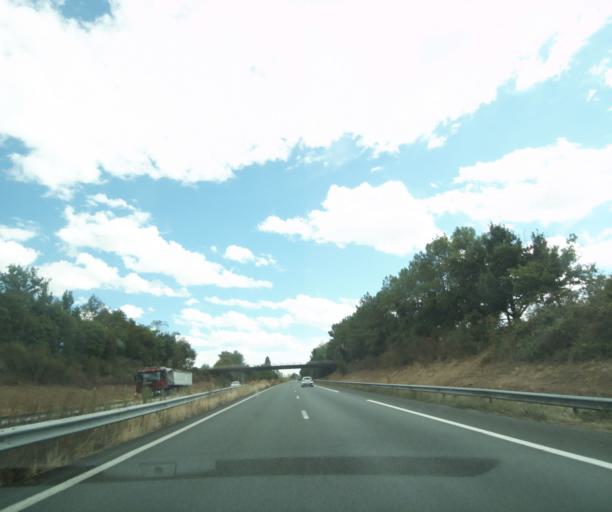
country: FR
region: Aquitaine
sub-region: Departement du Lot-et-Garonne
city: Meilhan-sur-Garonne
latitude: 44.4897
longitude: 0.0026
